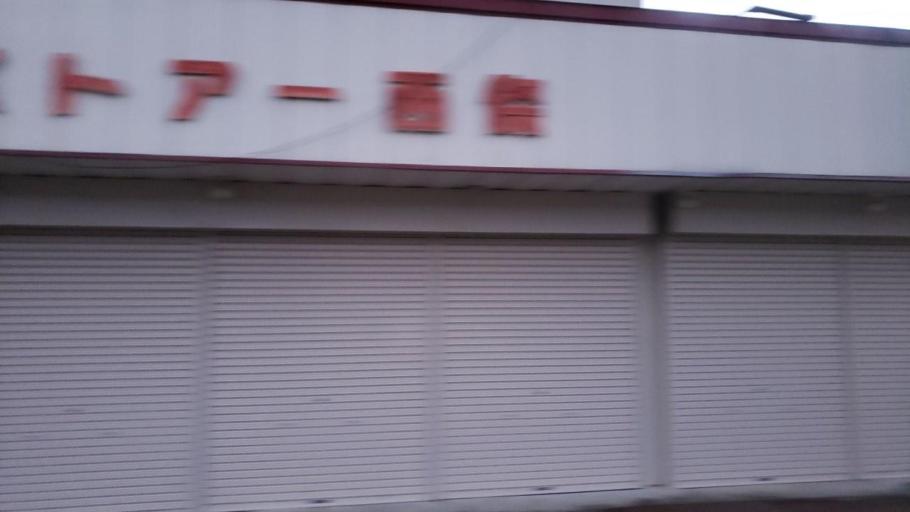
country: JP
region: Tokushima
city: Kamojimacho-jogejima
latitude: 34.1107
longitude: 134.3311
